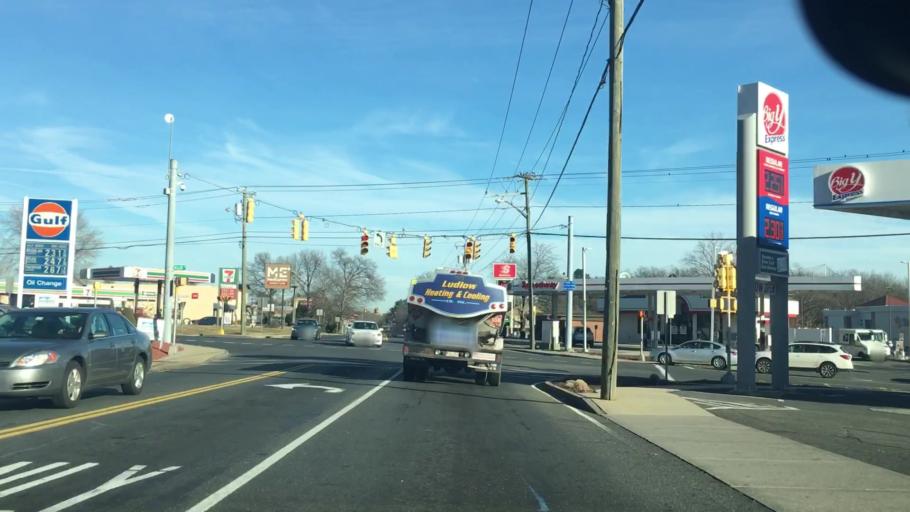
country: US
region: Massachusetts
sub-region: Hampden County
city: East Longmeadow
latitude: 42.0907
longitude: -72.5003
